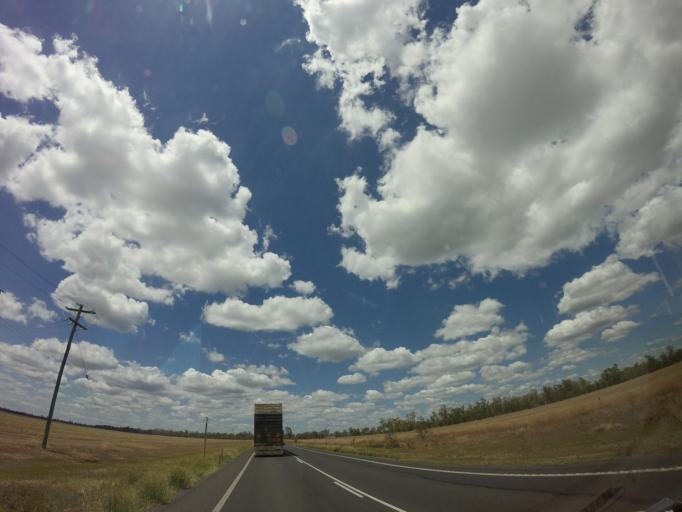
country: AU
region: Queensland
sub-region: Toowoomba
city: Oakey
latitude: -27.8159
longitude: 151.3575
